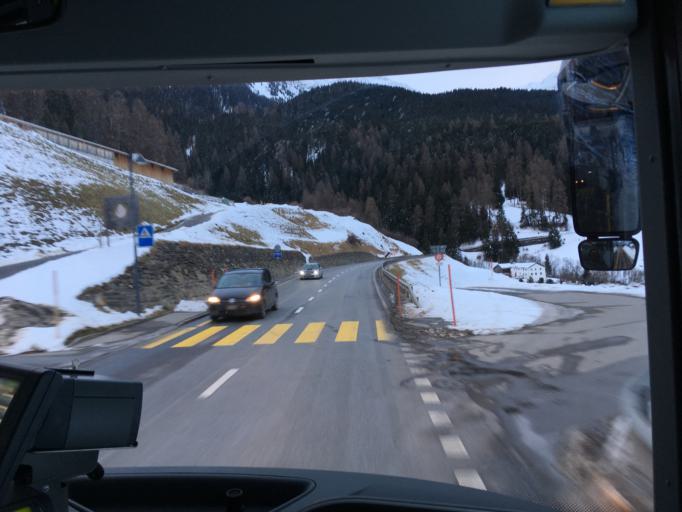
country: CH
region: Grisons
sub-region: Albula District
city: Tiefencastel
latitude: 46.5793
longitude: 9.6217
